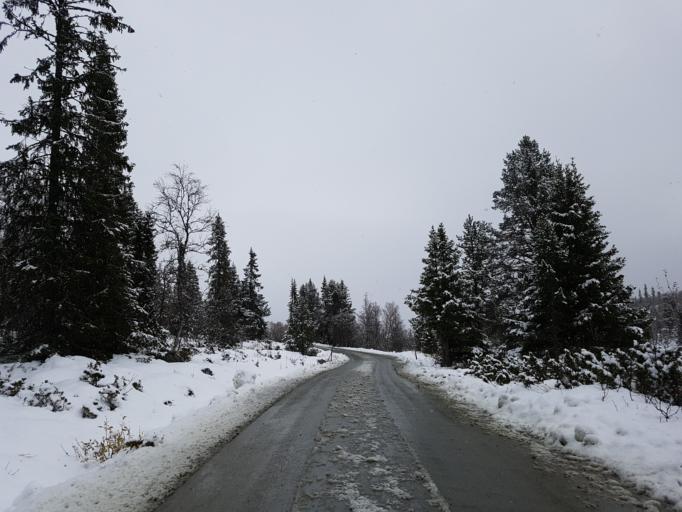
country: NO
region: Oppland
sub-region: Sel
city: Otta
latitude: 61.8029
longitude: 9.7008
